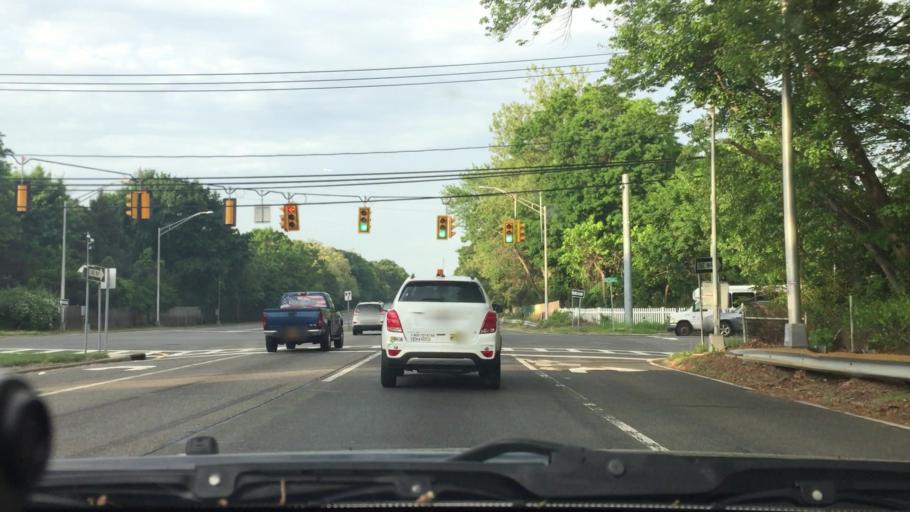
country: US
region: New York
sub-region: Suffolk County
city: Selden
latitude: 40.8754
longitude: -73.0214
